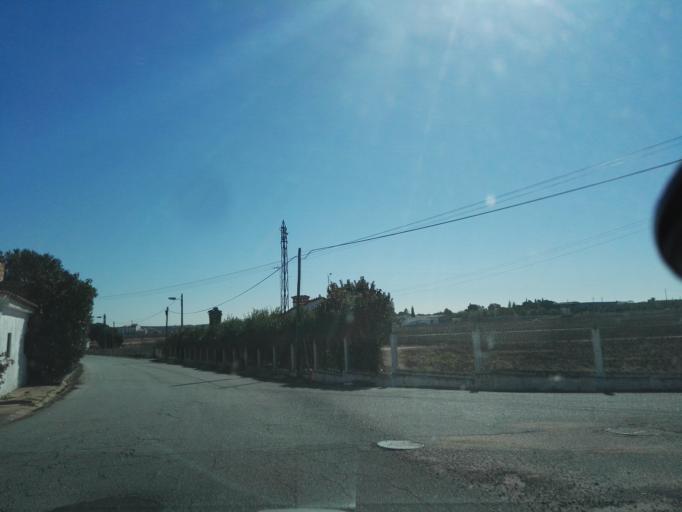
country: PT
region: Portalegre
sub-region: Elvas
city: Elvas
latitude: 38.8902
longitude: -7.1414
